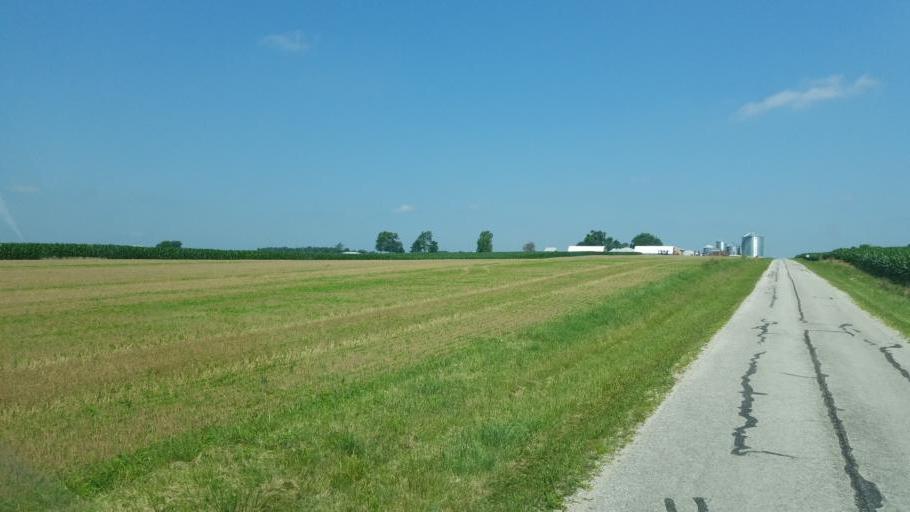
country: US
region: Ohio
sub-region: Sandusky County
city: Green Springs
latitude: 41.0902
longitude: -82.9768
